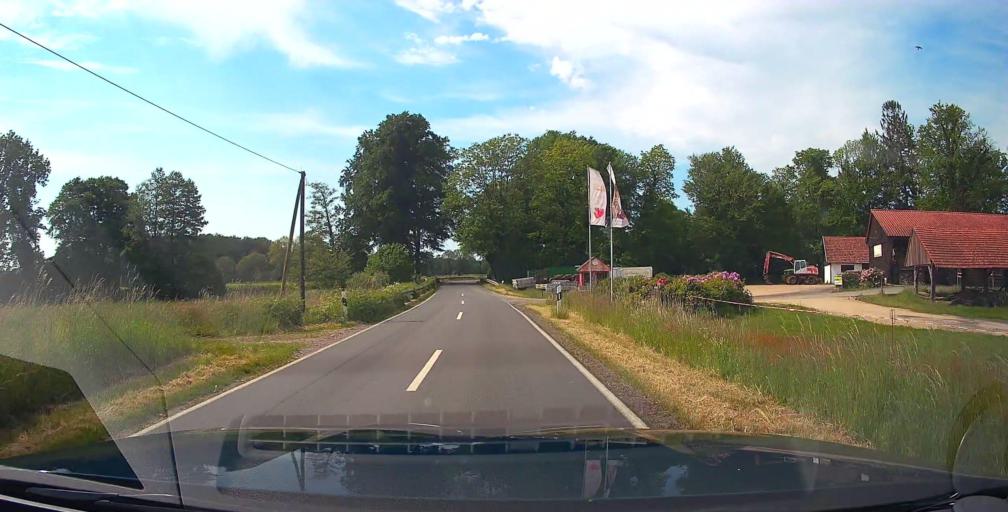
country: DE
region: North Rhine-Westphalia
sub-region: Regierungsbezirk Munster
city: Ladbergen
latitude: 52.1382
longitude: 7.7973
